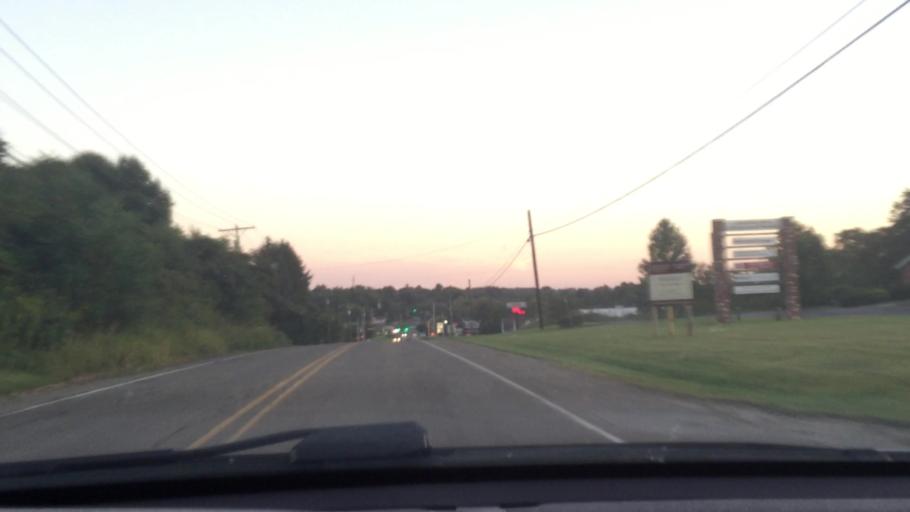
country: US
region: Pennsylvania
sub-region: Butler County
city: Slippery Rock
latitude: 41.0741
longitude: -80.0517
